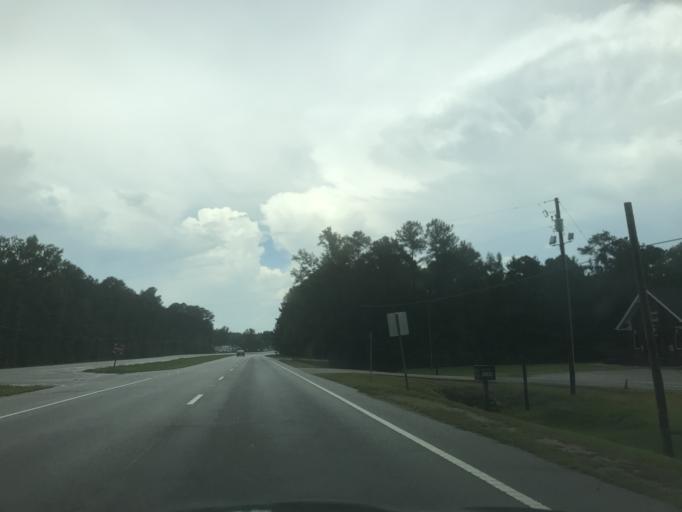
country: US
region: North Carolina
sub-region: Johnston County
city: Wilsons Mills
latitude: 35.5749
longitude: -78.3974
